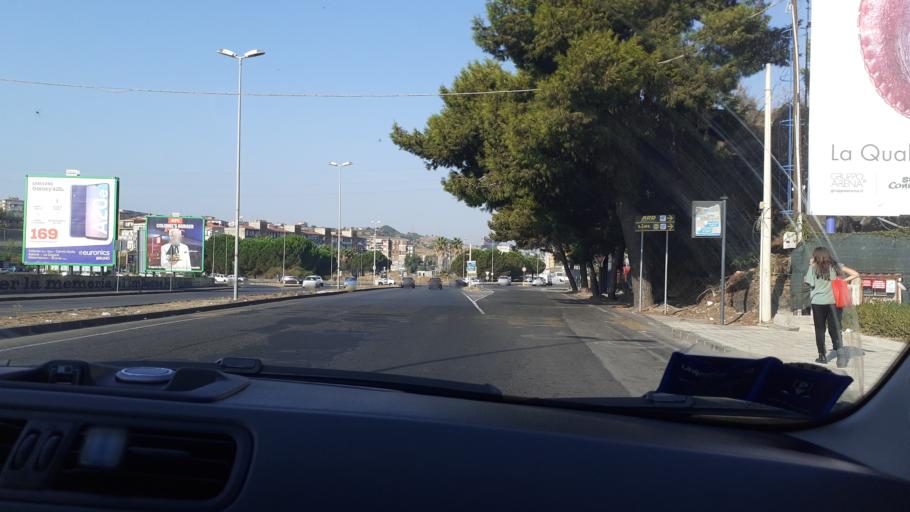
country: IT
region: Sicily
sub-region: Catania
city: Misterbianco
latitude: 37.5136
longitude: 15.0412
